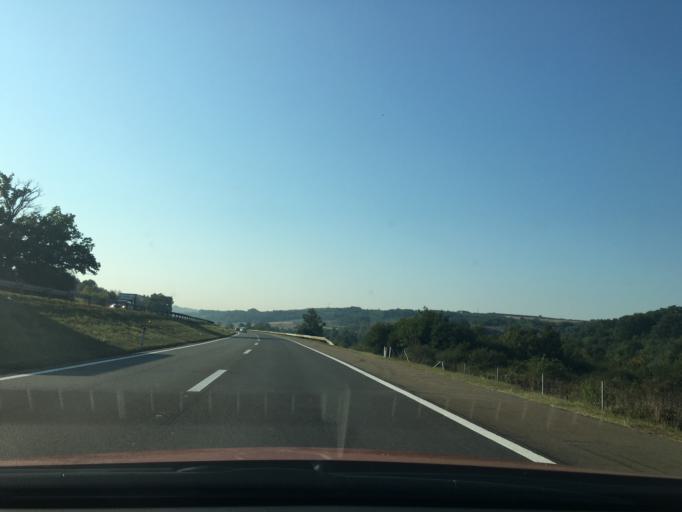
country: RS
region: Central Serbia
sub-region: Belgrade
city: Sopot
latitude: 44.5963
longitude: 20.6395
